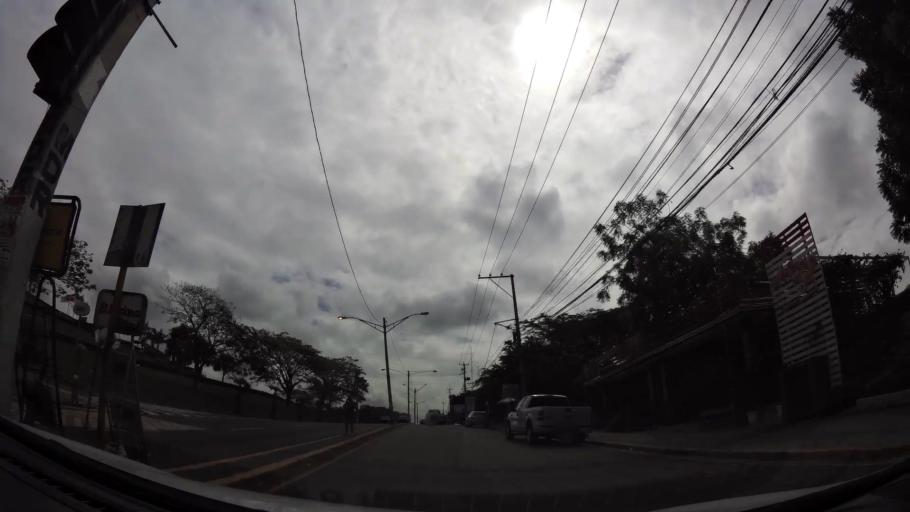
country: DO
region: Santiago
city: Santiago de los Caballeros
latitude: 19.4500
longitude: -70.6957
